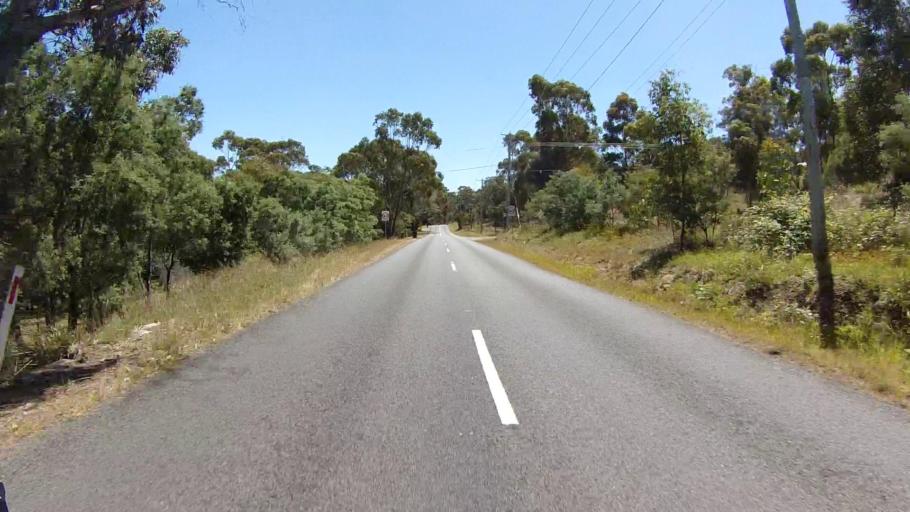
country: AU
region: Tasmania
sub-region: Clarence
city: Howrah
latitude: -42.8679
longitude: 147.4245
